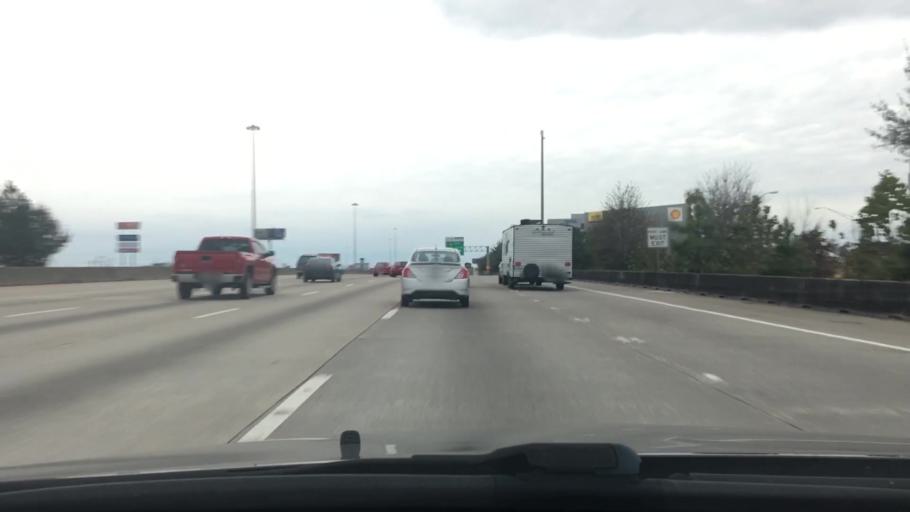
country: US
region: Texas
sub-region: Montgomery County
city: Oak Ridge North
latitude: 30.1283
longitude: -95.4437
